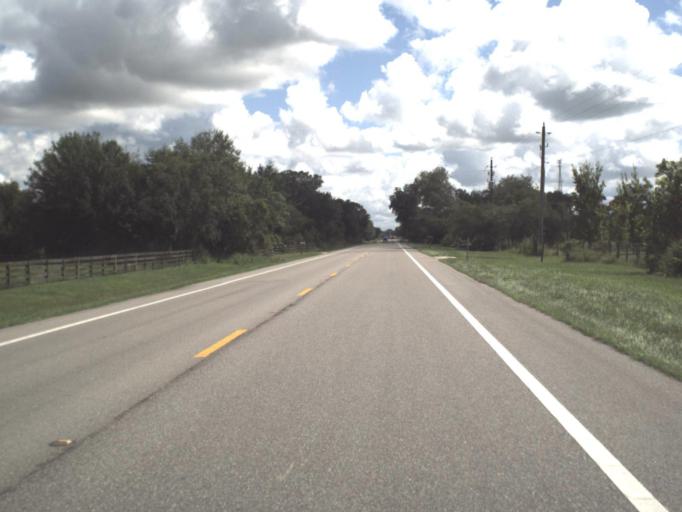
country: US
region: Florida
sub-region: Sarasota County
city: Lake Sarasota
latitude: 27.3609
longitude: -82.1955
